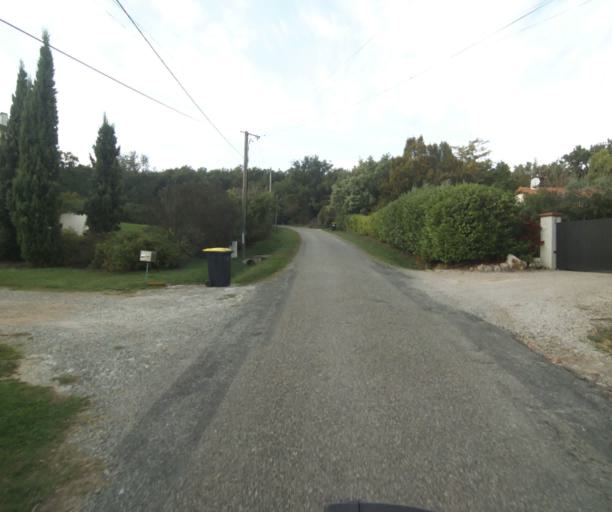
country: FR
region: Midi-Pyrenees
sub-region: Departement de la Haute-Garonne
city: Launac
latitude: 43.8108
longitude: 1.1087
